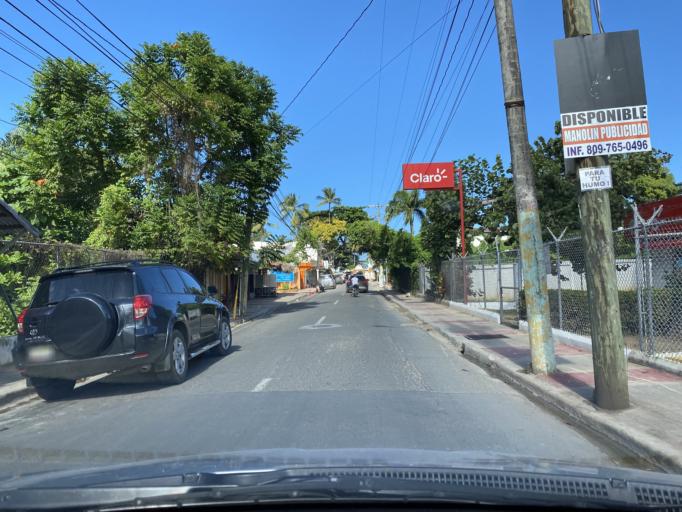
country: DO
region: Samana
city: Las Terrenas
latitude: 19.3202
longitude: -69.5387
